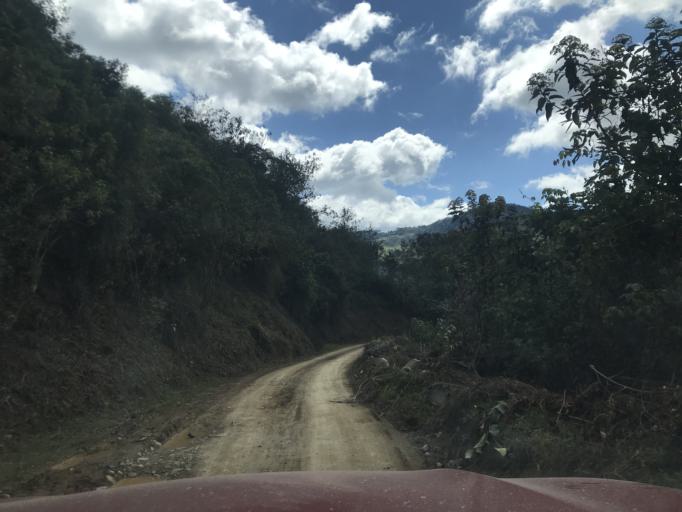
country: PE
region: Cajamarca
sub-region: Provincia de Chota
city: Querocoto
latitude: -6.3459
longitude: -79.0528
